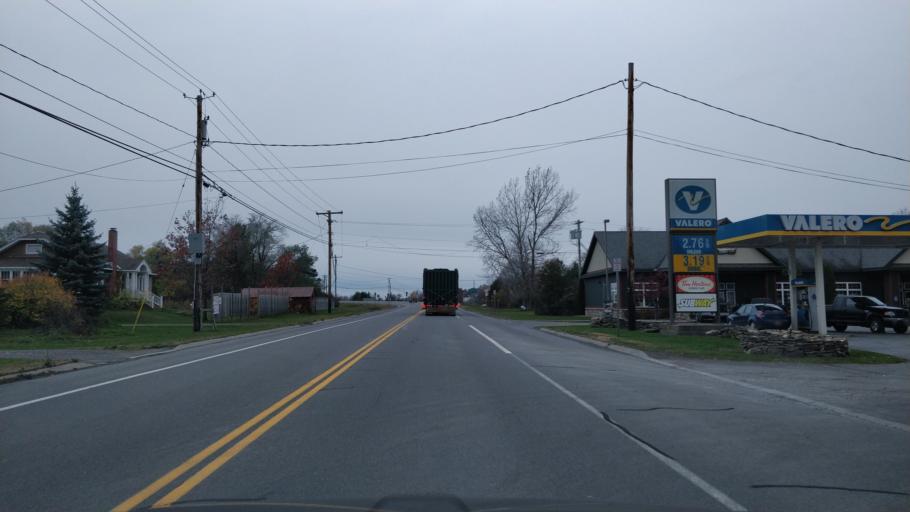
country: CA
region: Ontario
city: Brockville
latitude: 44.5946
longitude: -75.6353
